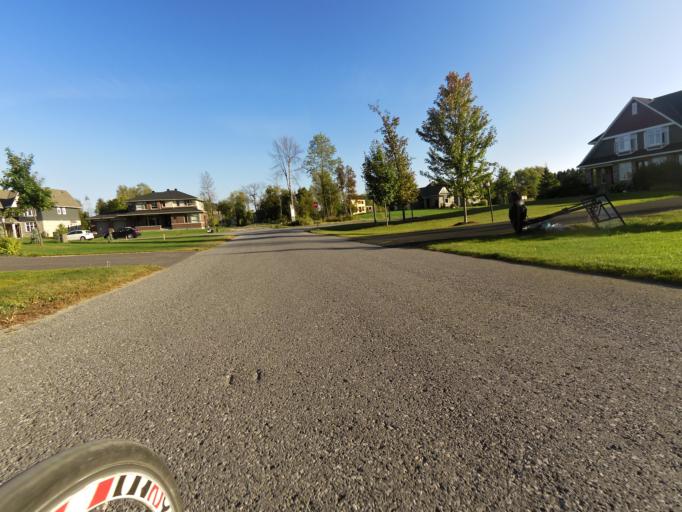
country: CA
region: Ontario
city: Bells Corners
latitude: 45.2142
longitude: -75.7079
